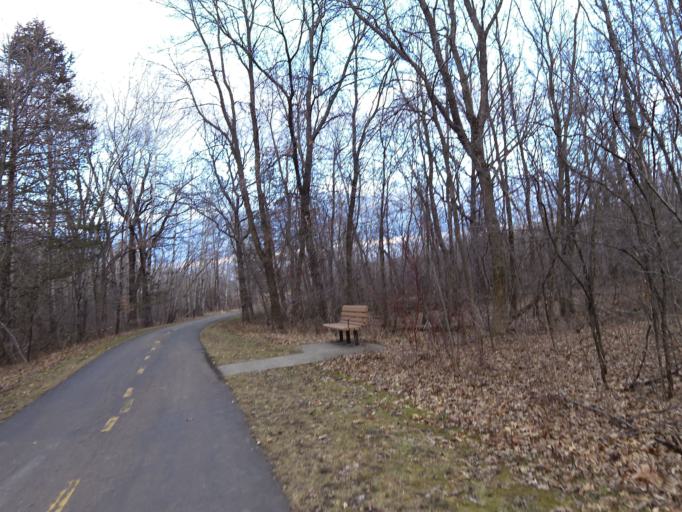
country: US
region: Minnesota
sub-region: Scott County
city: Prior Lake
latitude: 44.6872
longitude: -93.3899
